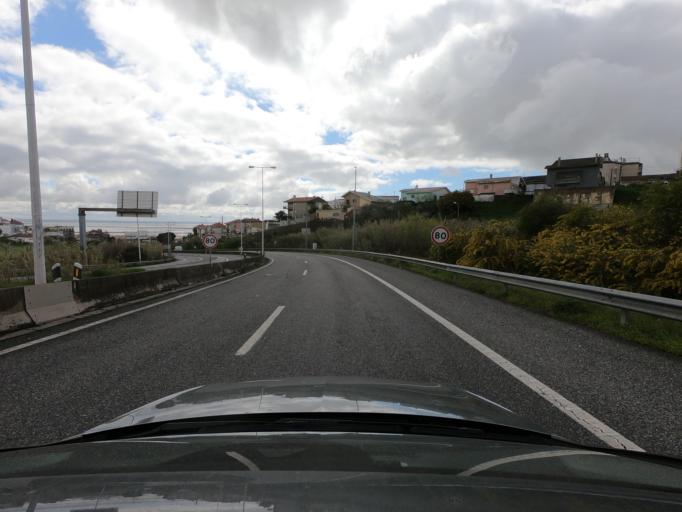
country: PT
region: Lisbon
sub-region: Loures
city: Santa Iria da Azoia
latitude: 38.8484
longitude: -9.0872
